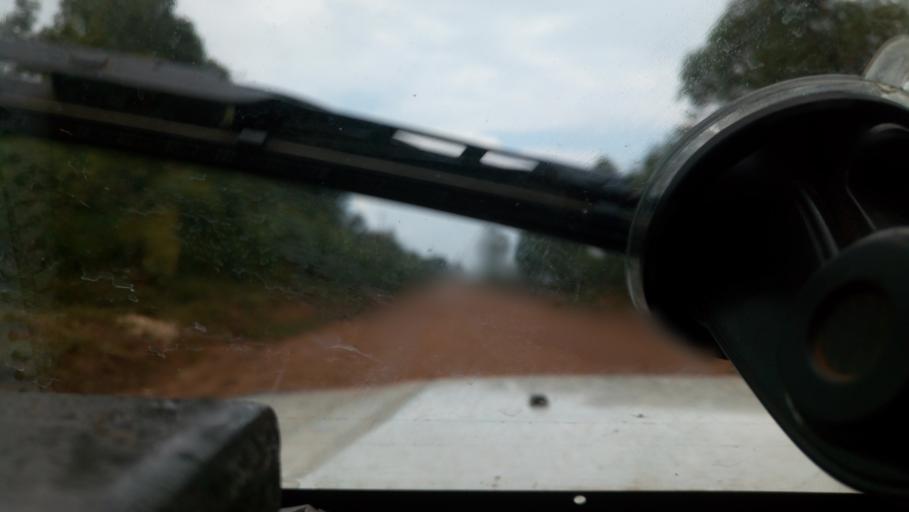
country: KE
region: Kisii
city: Ogembo
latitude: -0.8788
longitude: 34.5865
